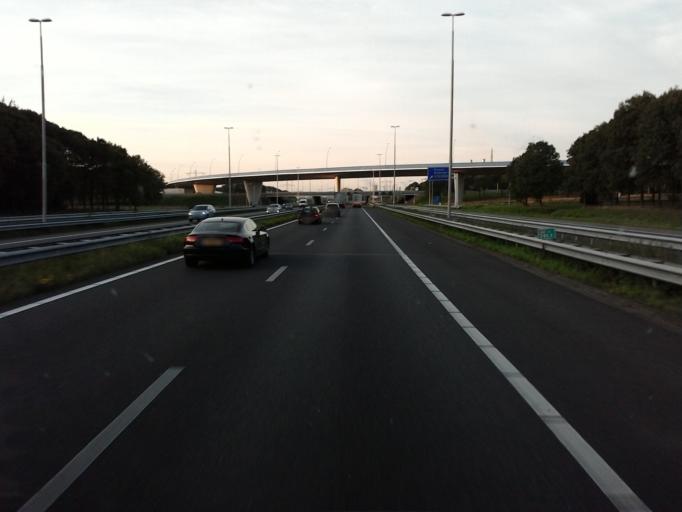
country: NL
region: Limburg
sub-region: Gemeente Stein
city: Stein
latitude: 50.9644
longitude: 5.7871
